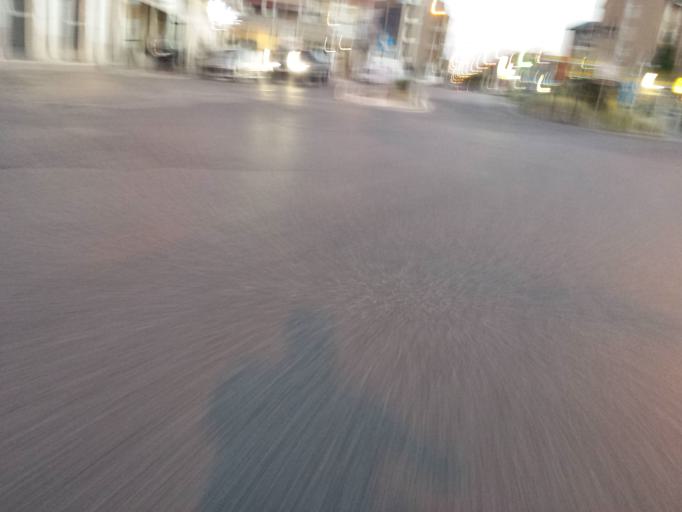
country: IT
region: Molise
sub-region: Provincia di Campobasso
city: Campobasso
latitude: 41.5700
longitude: 14.6745
